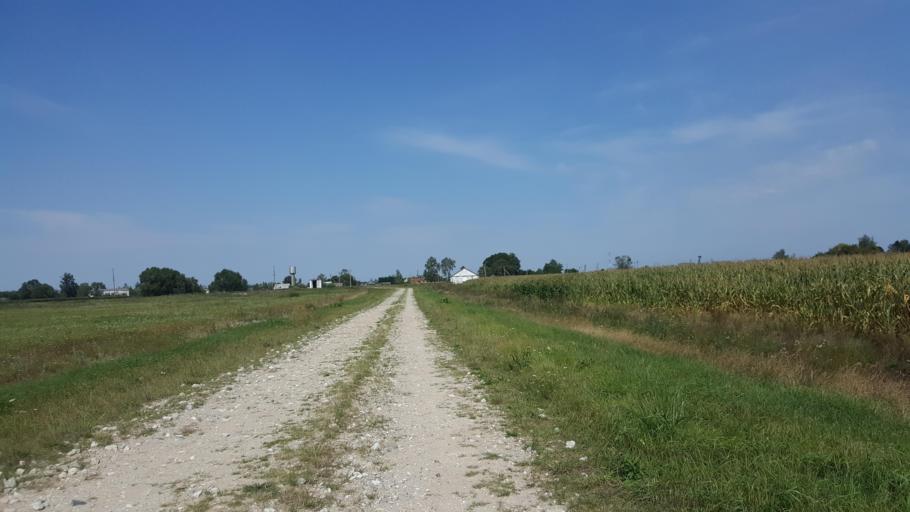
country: PL
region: Podlasie
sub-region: Powiat hajnowski
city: Czeremcha
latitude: 52.4899
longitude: 23.5729
